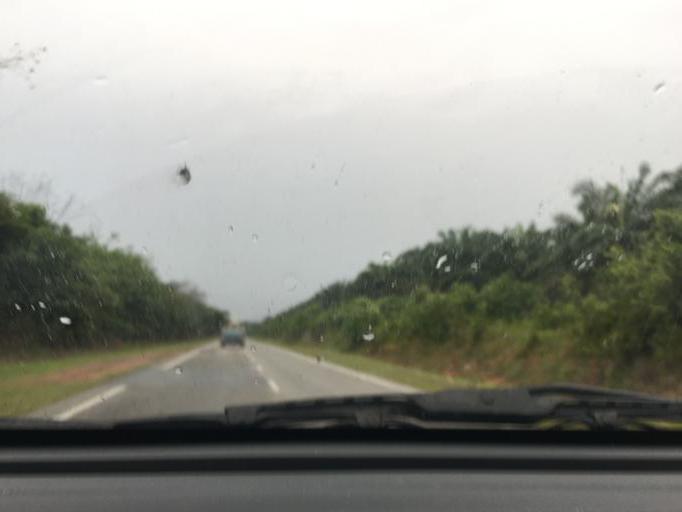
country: MY
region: Kedah
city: Sungai Petani
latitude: 5.6198
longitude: 100.6386
